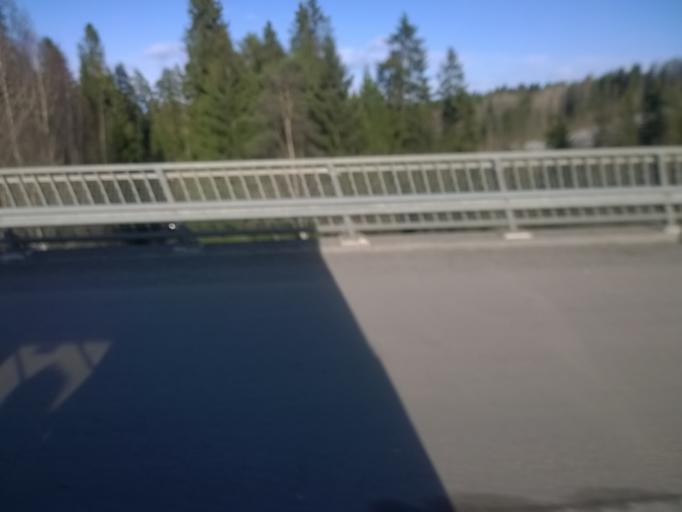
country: FI
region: Pirkanmaa
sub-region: Tampere
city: Tampere
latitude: 61.4610
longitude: 23.8453
